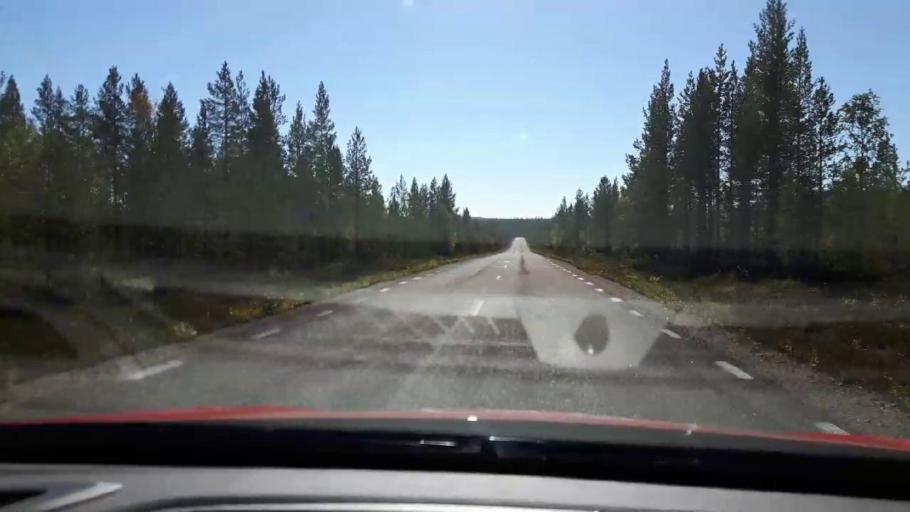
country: SE
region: Jaemtland
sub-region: Harjedalens Kommun
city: Sveg
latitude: 61.7189
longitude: 14.1682
